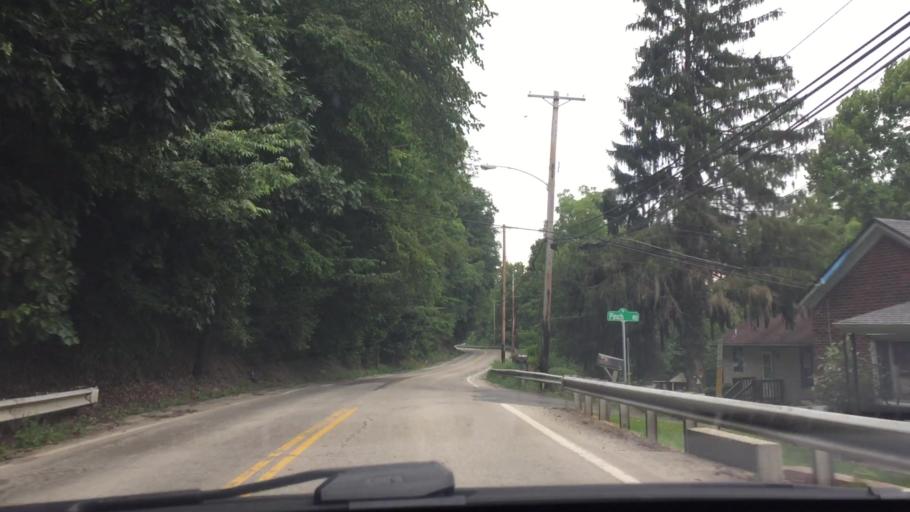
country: US
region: Pennsylvania
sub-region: Allegheny County
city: Rennerdale
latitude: 40.3774
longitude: -80.1400
